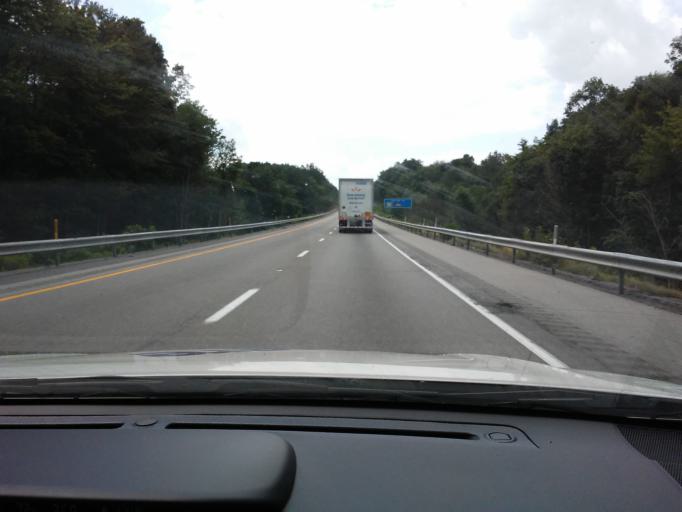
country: US
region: Pennsylvania
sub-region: Centre County
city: Milesburg
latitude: 41.0251
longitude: -77.9170
